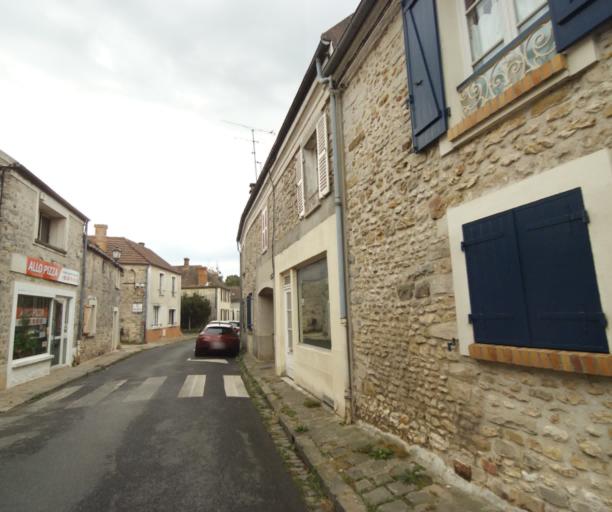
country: FR
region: Ile-de-France
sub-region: Departement de l'Essonne
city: Soisy-sur-Ecole
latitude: 48.4760
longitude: 2.4929
